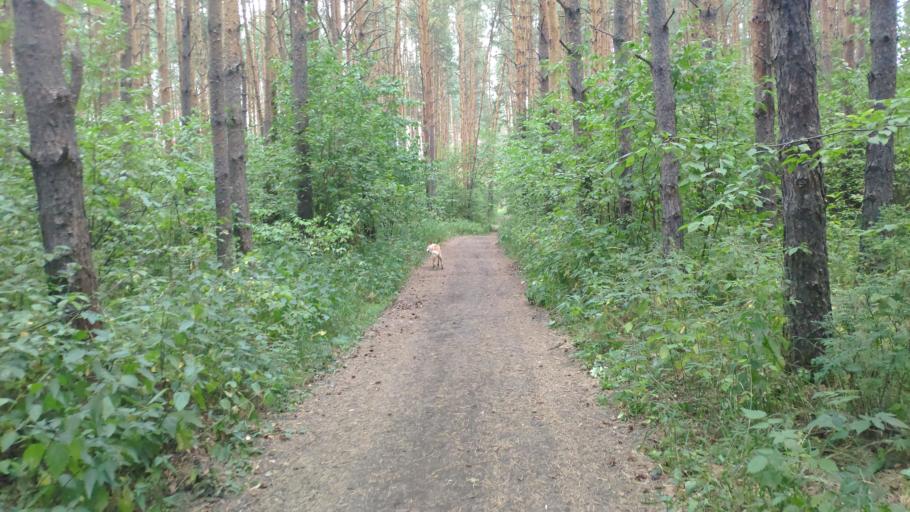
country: RU
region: Bashkortostan
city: Abzakovo
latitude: 53.8093
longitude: 58.6395
